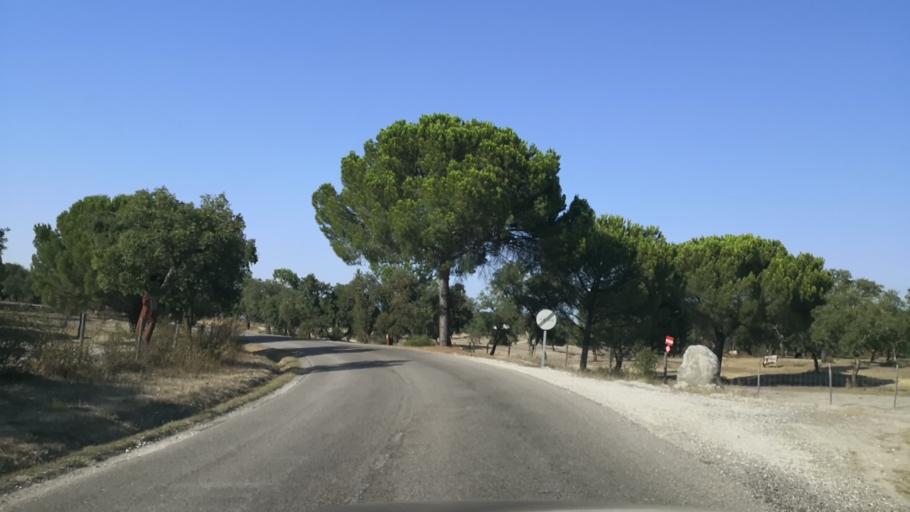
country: PT
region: Santarem
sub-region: Coruche
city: Coruche
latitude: 38.8501
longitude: -8.5449
